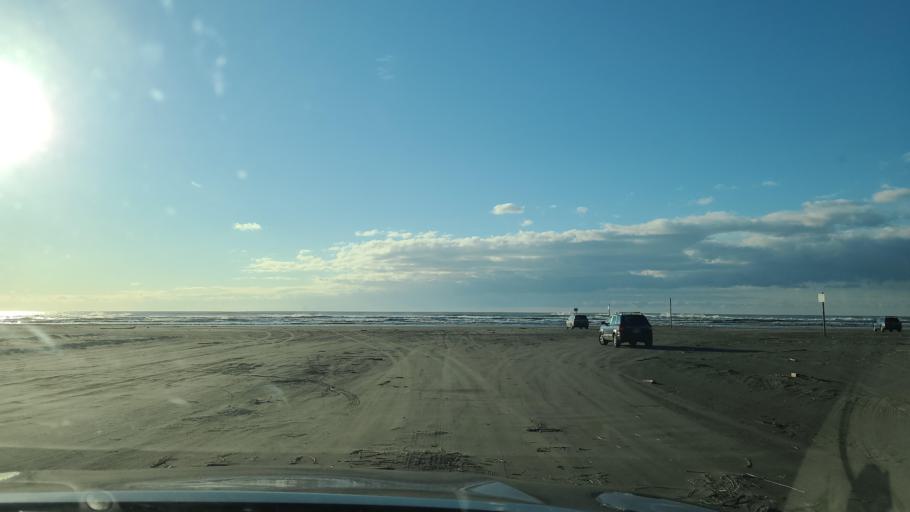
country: US
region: Washington
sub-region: Grays Harbor County
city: Ocean Shores
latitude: 46.9940
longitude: -124.1736
